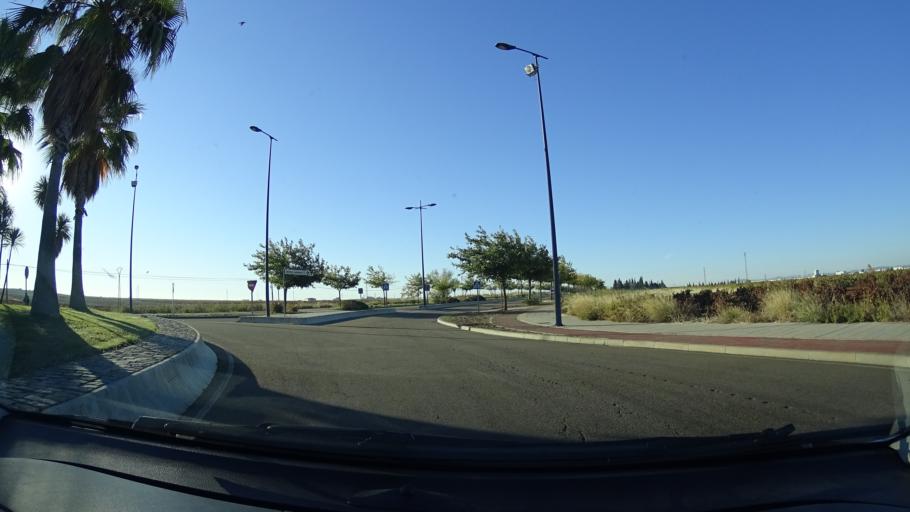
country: ES
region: Extremadura
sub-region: Provincia de Badajoz
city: Almendralejo
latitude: 38.7045
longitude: -6.4016
